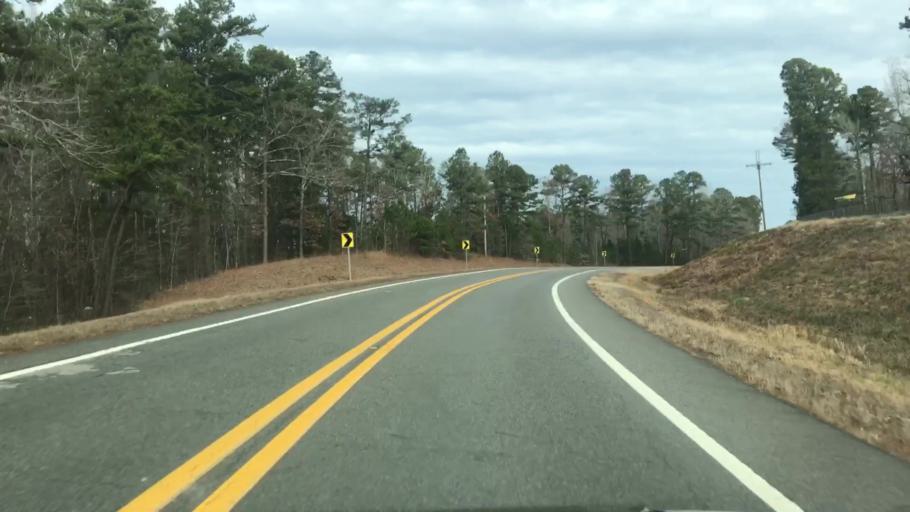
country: US
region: Arkansas
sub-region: Montgomery County
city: Mount Ida
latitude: 34.6129
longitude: -93.7032
